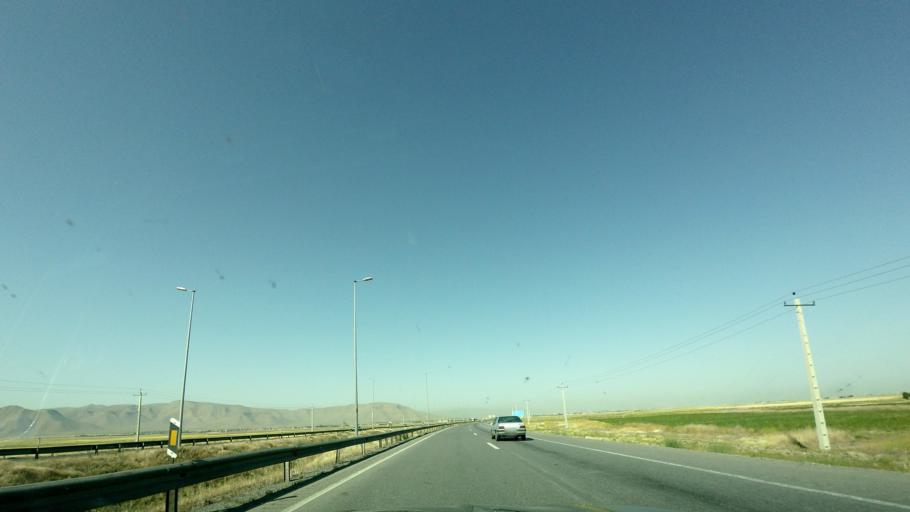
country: IR
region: Markazi
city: Arak
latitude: 34.1662
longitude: 50.0294
